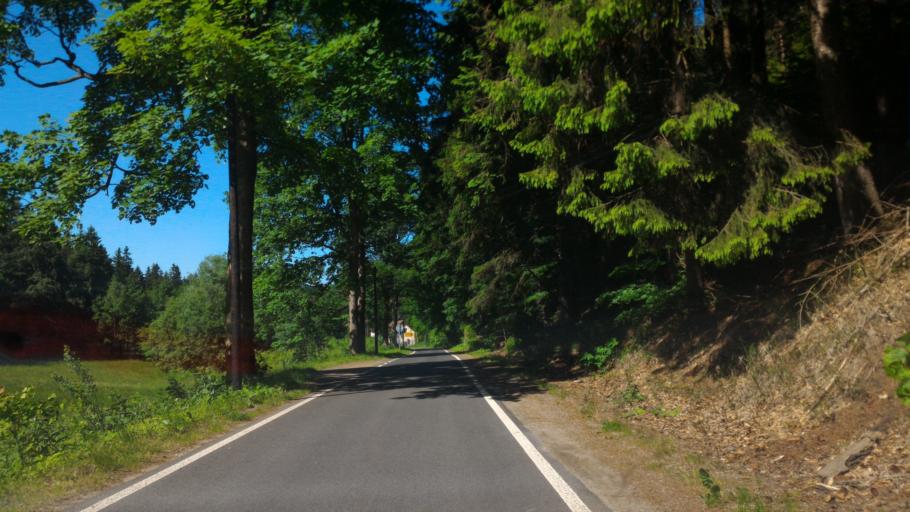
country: DE
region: Saxony
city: Kurort Jonsdorf
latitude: 50.8393
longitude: 14.7061
